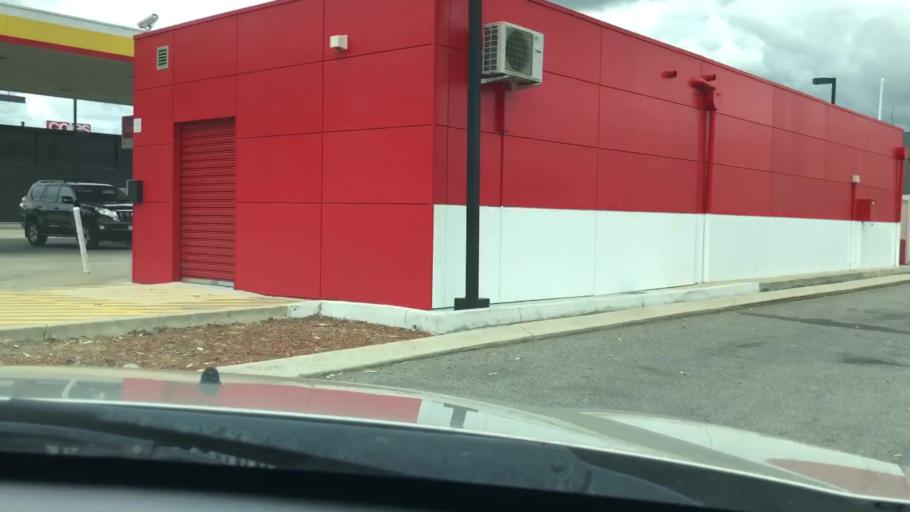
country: AU
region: Western Australia
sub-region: Armadale
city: Seville Grove
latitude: -32.1474
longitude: 115.9851
